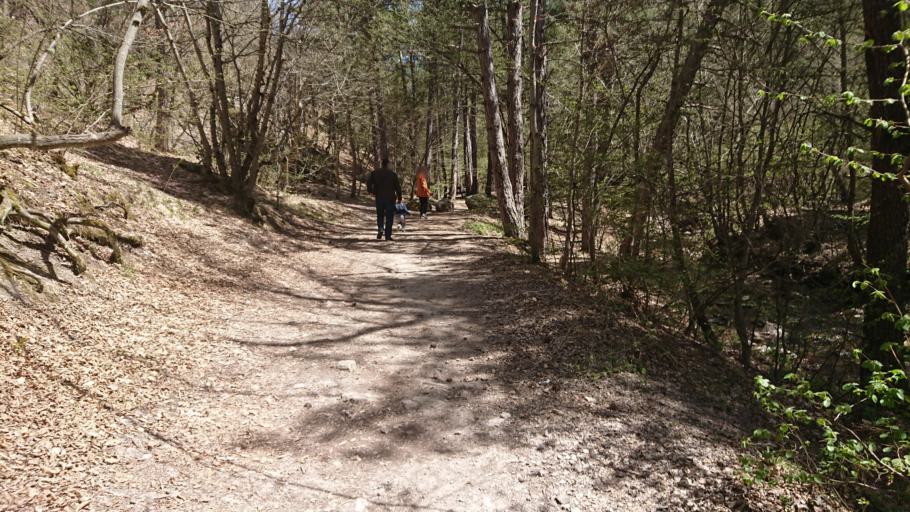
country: TR
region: Kuetahya
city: Sabuncu
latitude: 39.5094
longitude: 30.4205
